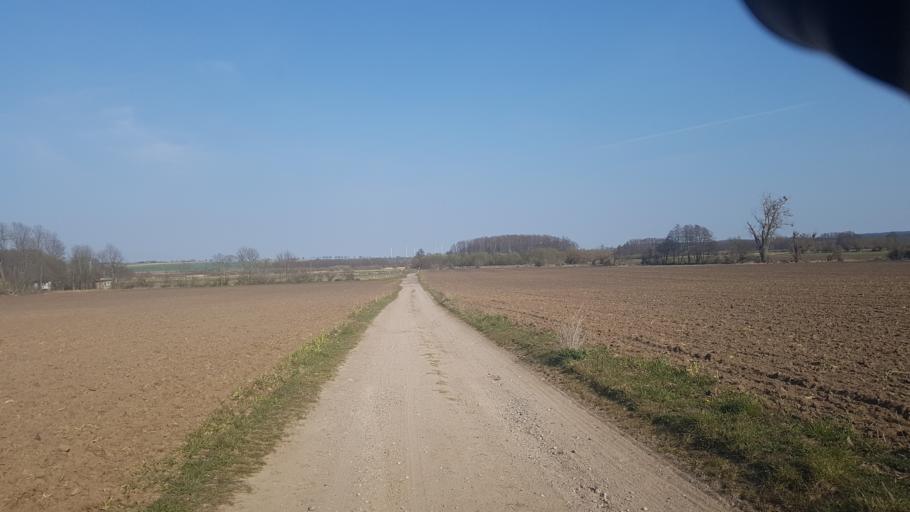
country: DE
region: Brandenburg
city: Prenzlau
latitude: 53.2243
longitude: 13.8451
